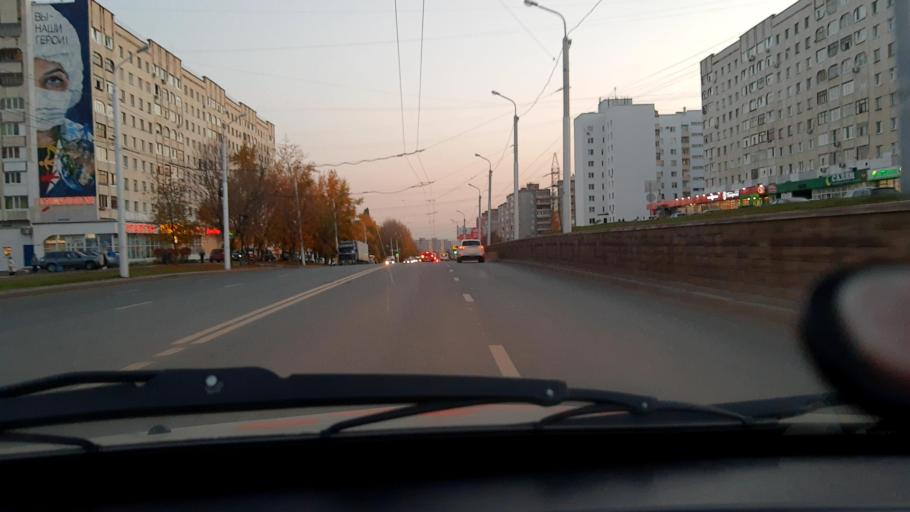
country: RU
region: Bashkortostan
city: Ufa
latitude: 54.7058
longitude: 55.9981
